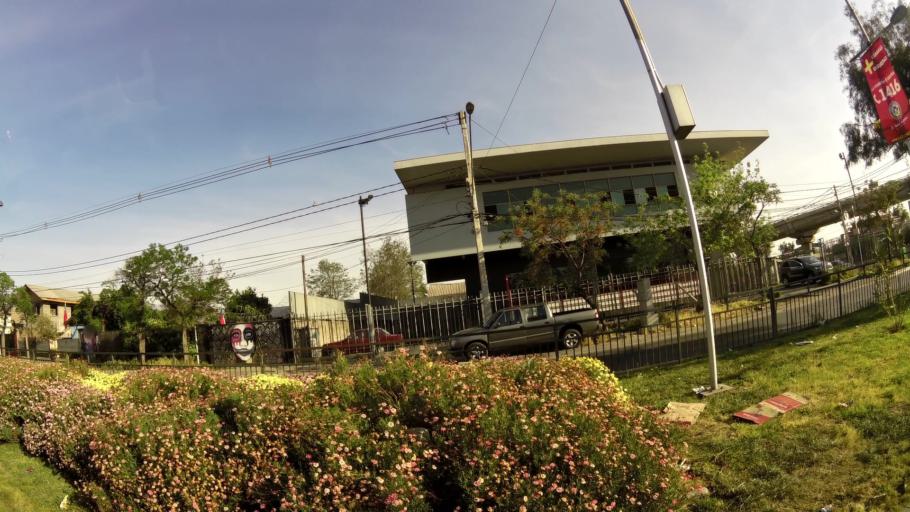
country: CL
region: Santiago Metropolitan
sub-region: Provincia de Santiago
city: La Pintana
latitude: -33.5472
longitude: -70.5871
